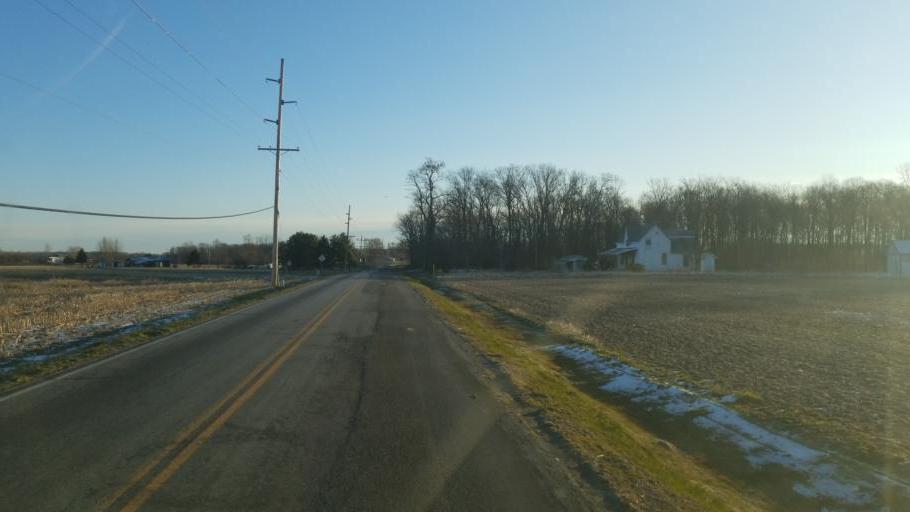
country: US
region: Ohio
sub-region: Highland County
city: Leesburg
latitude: 39.2447
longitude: -83.4842
